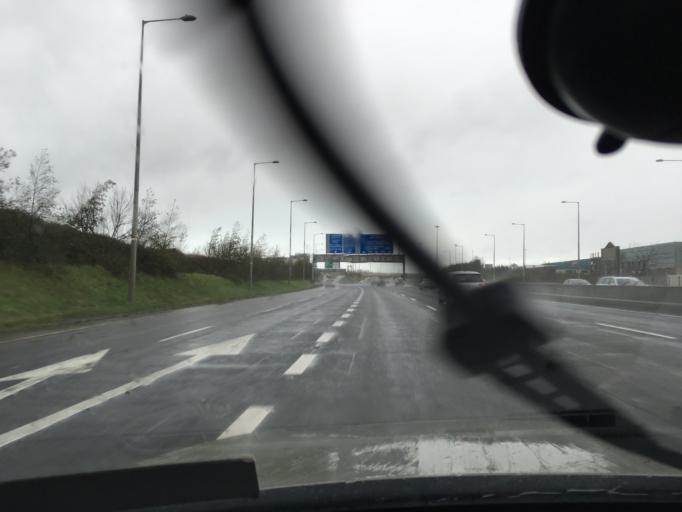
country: IE
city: Cherry Orchard
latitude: 53.3132
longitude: -6.3636
